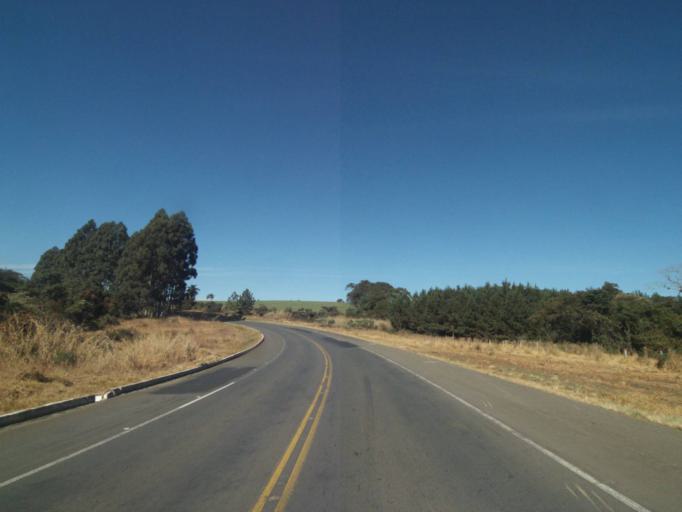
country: BR
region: Parana
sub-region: Tibagi
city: Tibagi
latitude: -24.7876
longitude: -50.4699
